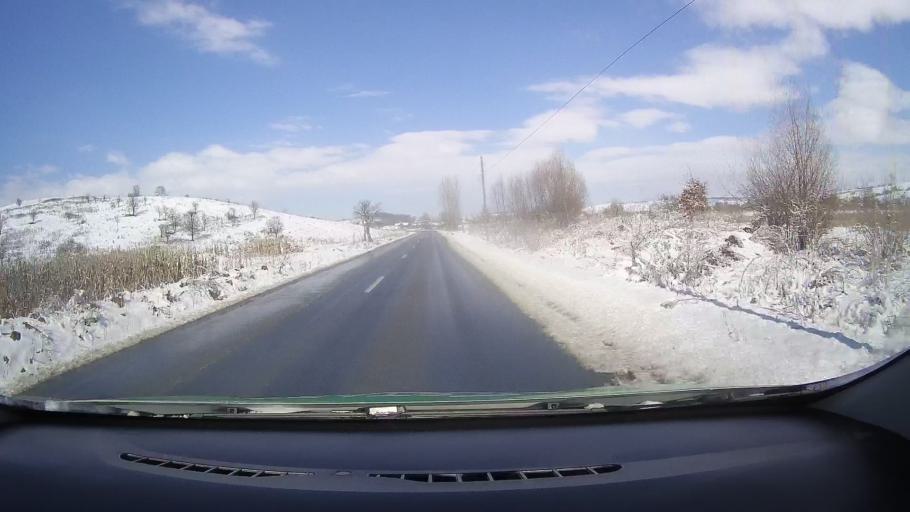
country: RO
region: Sibiu
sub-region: Comuna Nocrich
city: Nocrich
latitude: 45.8799
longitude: 24.4518
